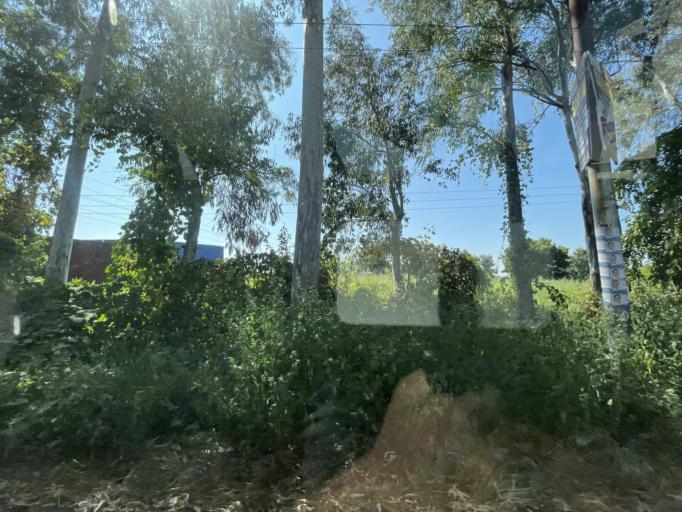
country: IN
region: Uttarakhand
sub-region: Naini Tal
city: Haldwani
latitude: 29.2122
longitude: 79.4589
